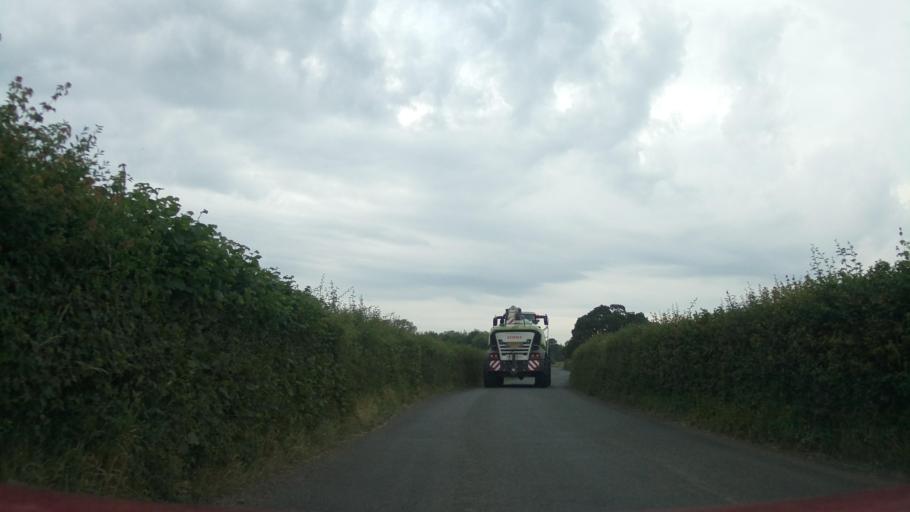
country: GB
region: England
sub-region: Somerset
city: Yeovil
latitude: 50.9130
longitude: -2.5826
